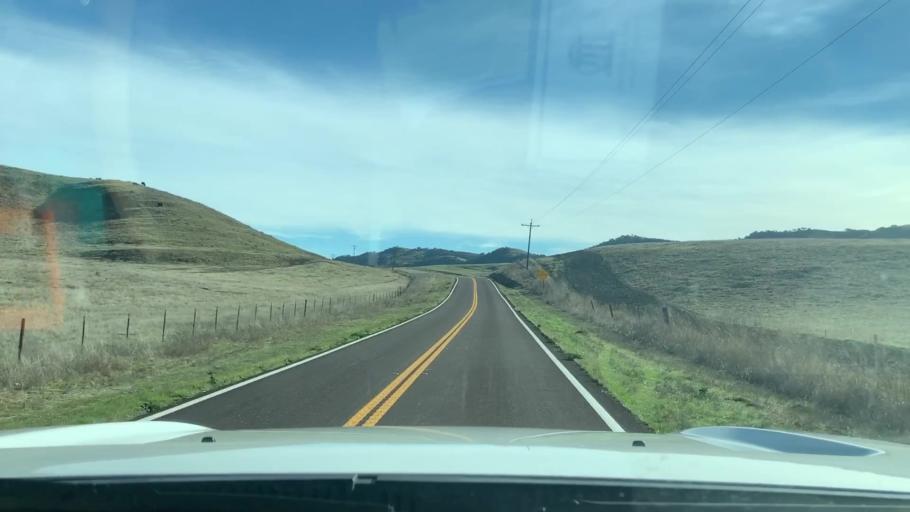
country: US
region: California
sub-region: Monterey County
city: King City
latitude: 36.1653
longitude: -120.8676
